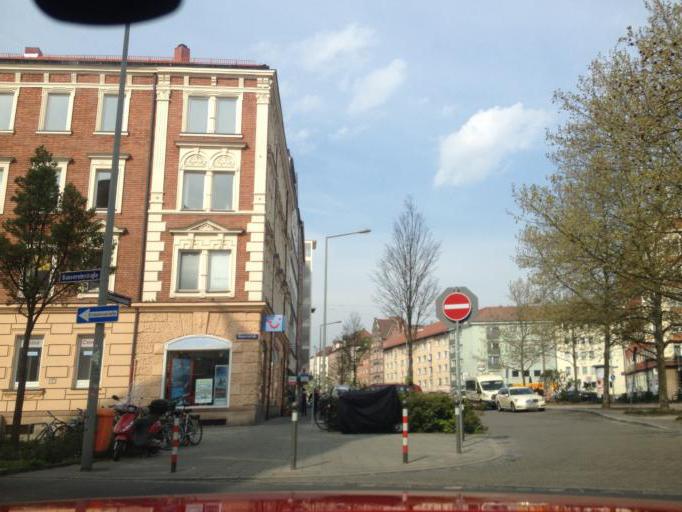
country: DE
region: Bavaria
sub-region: Regierungsbezirk Mittelfranken
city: Nuernberg
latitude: 49.4586
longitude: 11.0976
